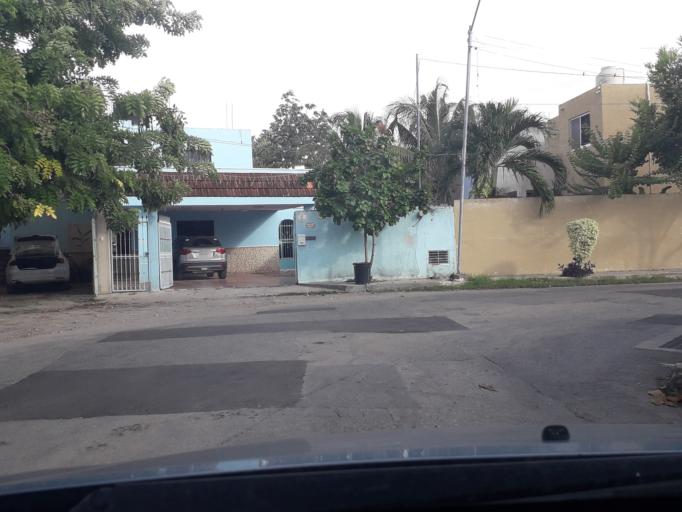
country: MX
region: Yucatan
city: Merida
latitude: 21.0064
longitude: -89.6394
